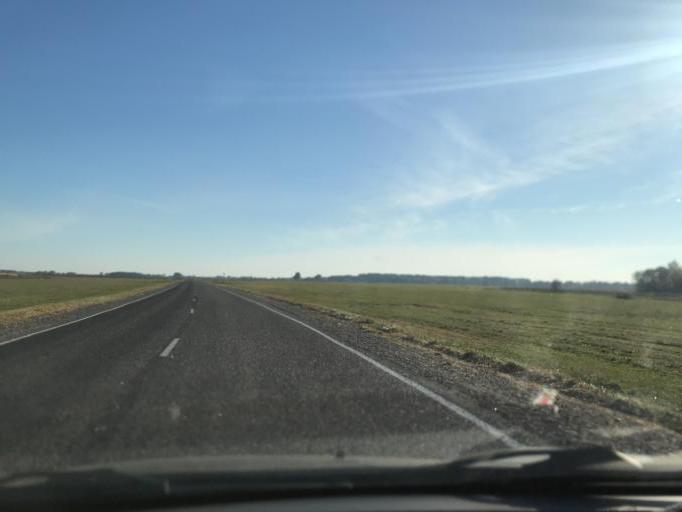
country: BY
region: Gomel
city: Brahin
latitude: 51.7728
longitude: 30.2761
